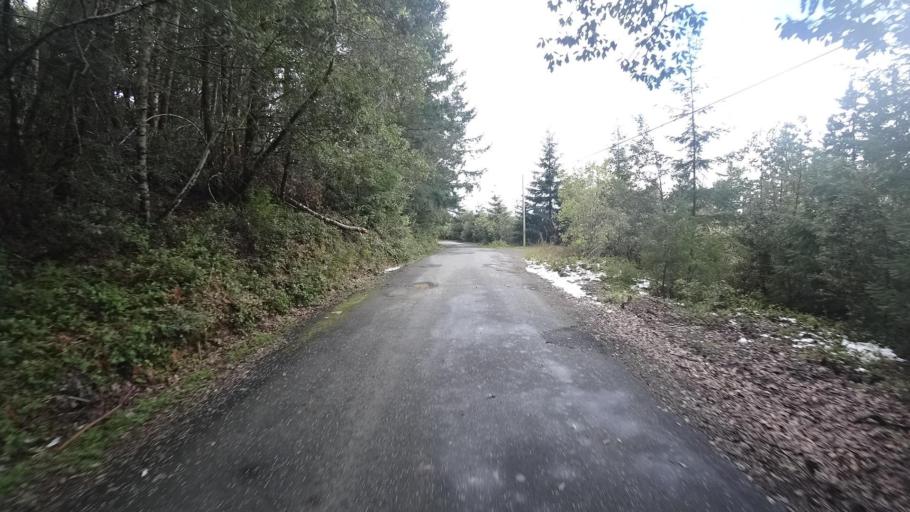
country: US
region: California
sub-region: Humboldt County
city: Blue Lake
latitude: 40.8725
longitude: -123.8921
